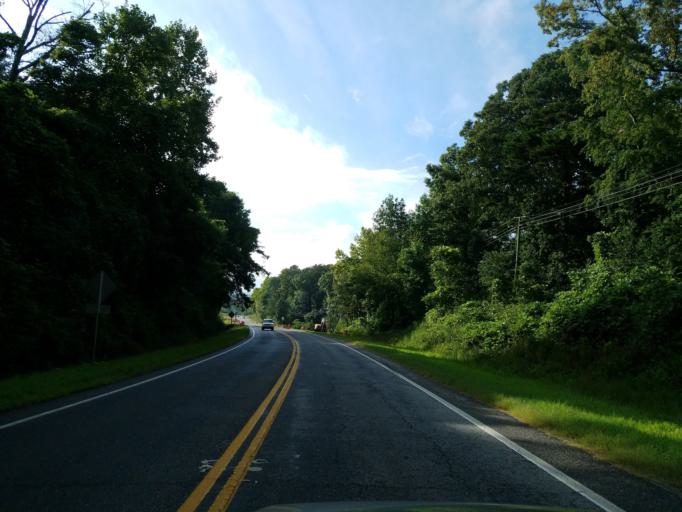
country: US
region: Georgia
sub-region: White County
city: Cleveland
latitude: 34.6081
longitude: -83.7711
